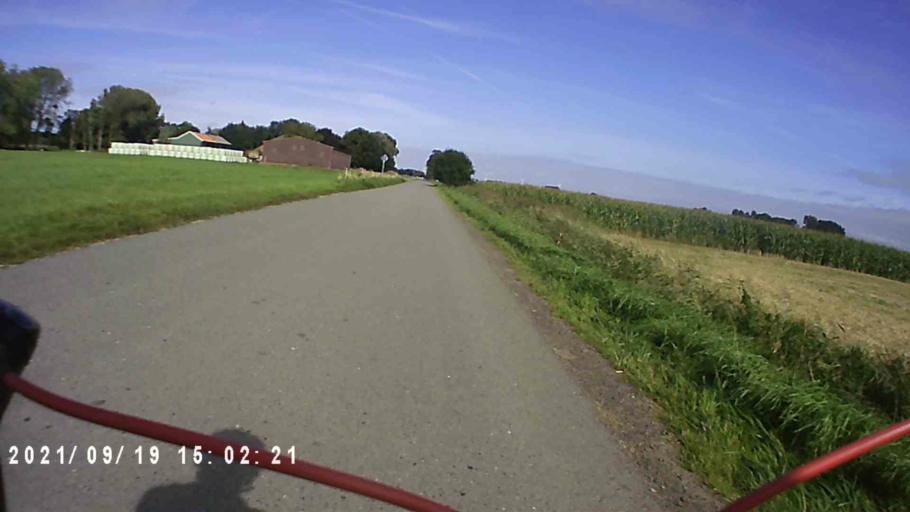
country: DE
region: Lower Saxony
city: Bunde
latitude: 53.1599
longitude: 7.2017
